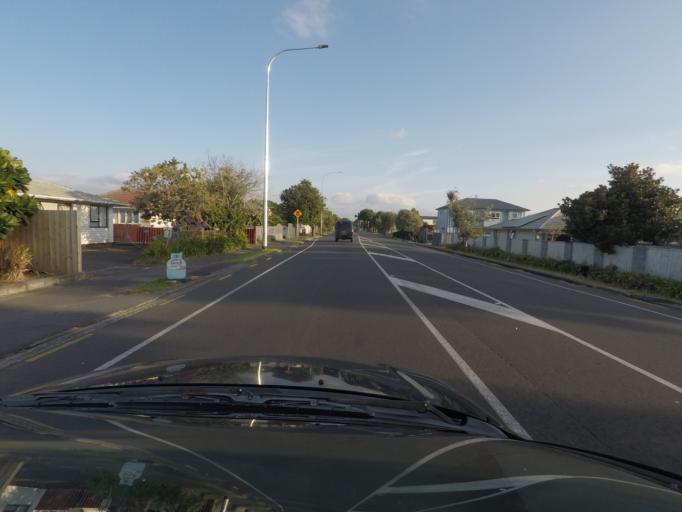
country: NZ
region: Auckland
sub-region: Auckland
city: Rosebank
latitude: -36.8861
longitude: 174.6841
